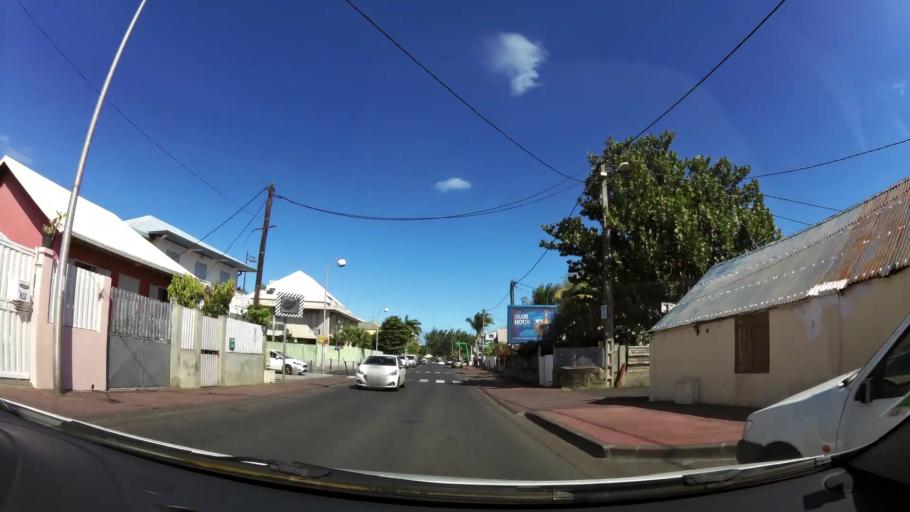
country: RE
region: Reunion
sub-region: Reunion
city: Saint-Pierre
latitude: -21.3367
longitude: 55.4593
